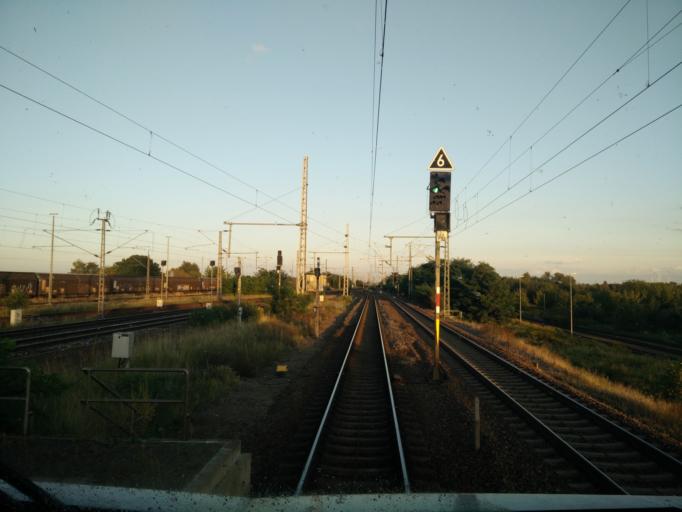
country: DE
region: Brandenburg
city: Nauen
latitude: 52.6119
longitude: 12.8882
